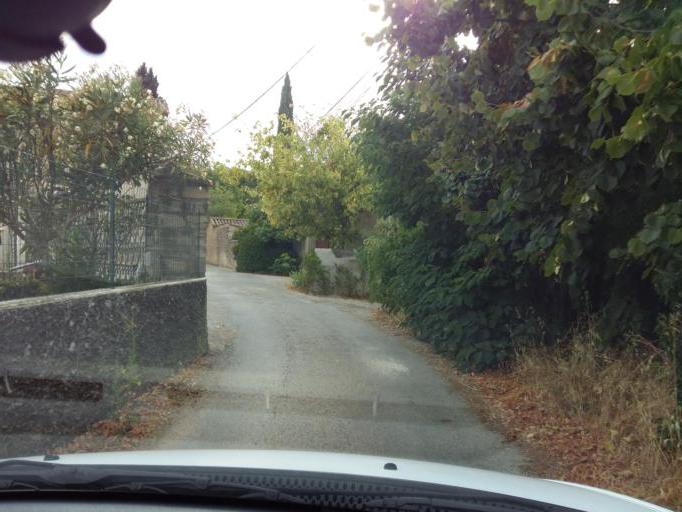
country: FR
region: Provence-Alpes-Cote d'Azur
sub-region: Departement du Vaucluse
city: Saint-Didier
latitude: 44.0075
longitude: 5.1094
